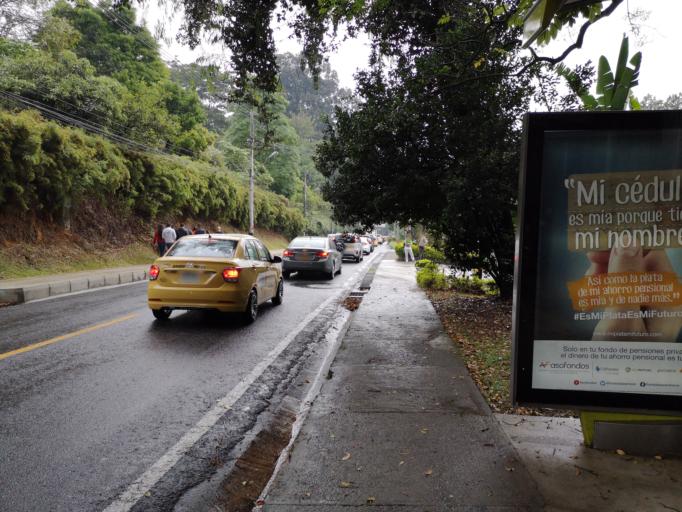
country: CO
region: Antioquia
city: Medellin
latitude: 6.2088
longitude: -75.5614
